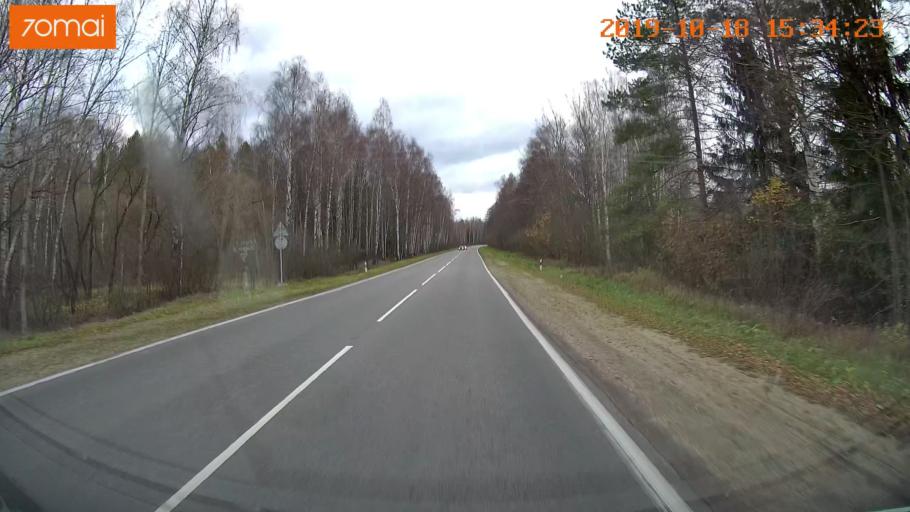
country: RU
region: Vladimir
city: Anopino
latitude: 55.8538
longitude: 40.6432
